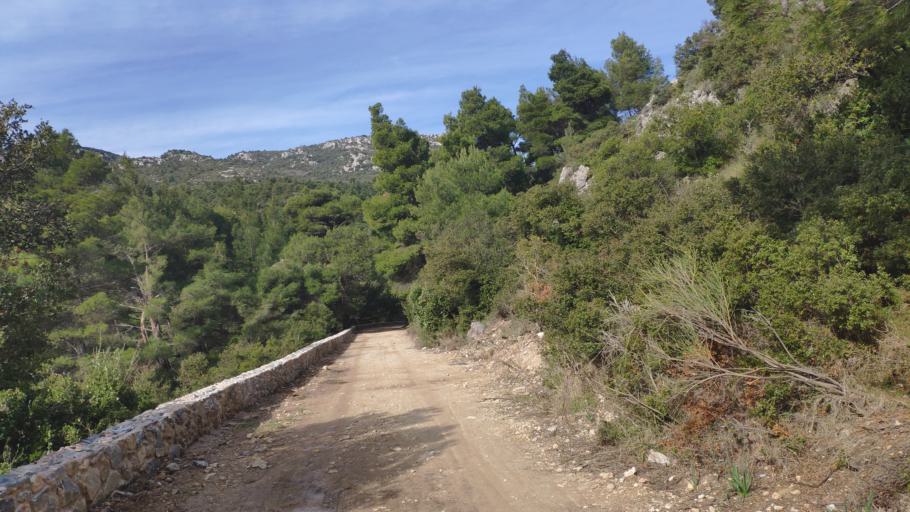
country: GR
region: Attica
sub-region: Nomarchia Anatolikis Attikis
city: Varybobi
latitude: 38.1646
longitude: 23.7822
